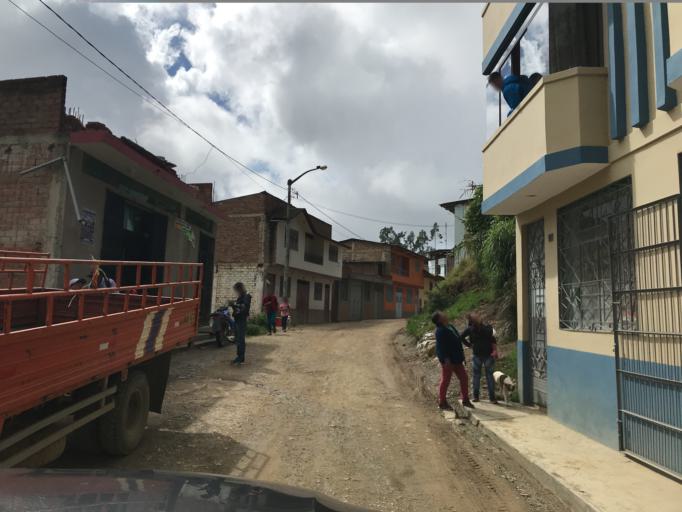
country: PE
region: Cajamarca
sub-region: Provincia de Chota
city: Querocoto
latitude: -6.3569
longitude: -79.0360
